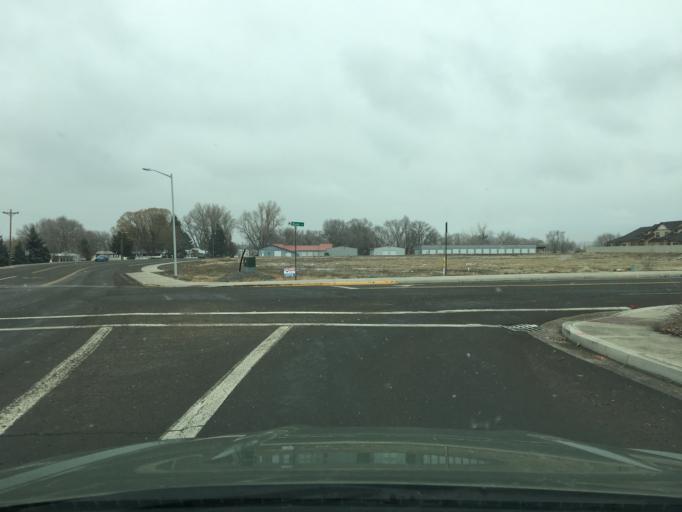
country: US
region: Colorado
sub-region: Montrose County
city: Montrose
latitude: 38.4815
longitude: -107.8567
